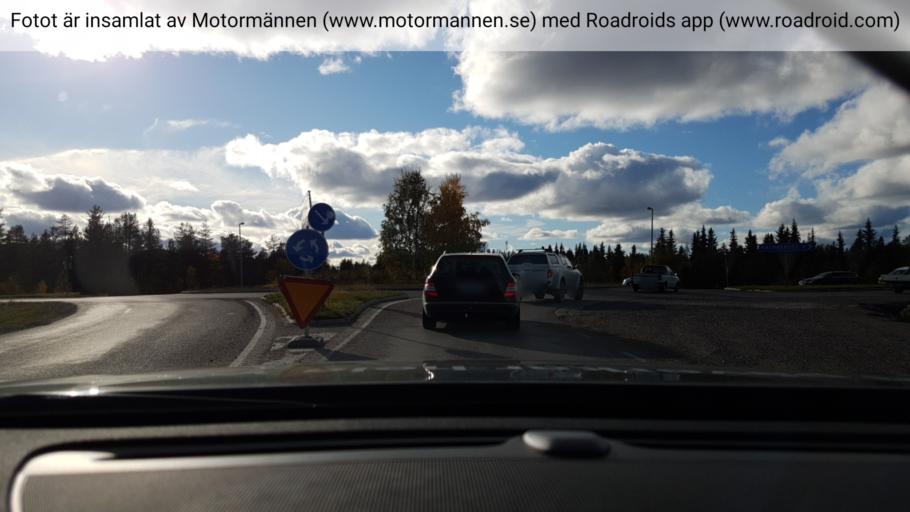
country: SE
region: Norrbotten
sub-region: Gallivare Kommun
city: Malmberget
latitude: 67.1603
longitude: 20.6583
